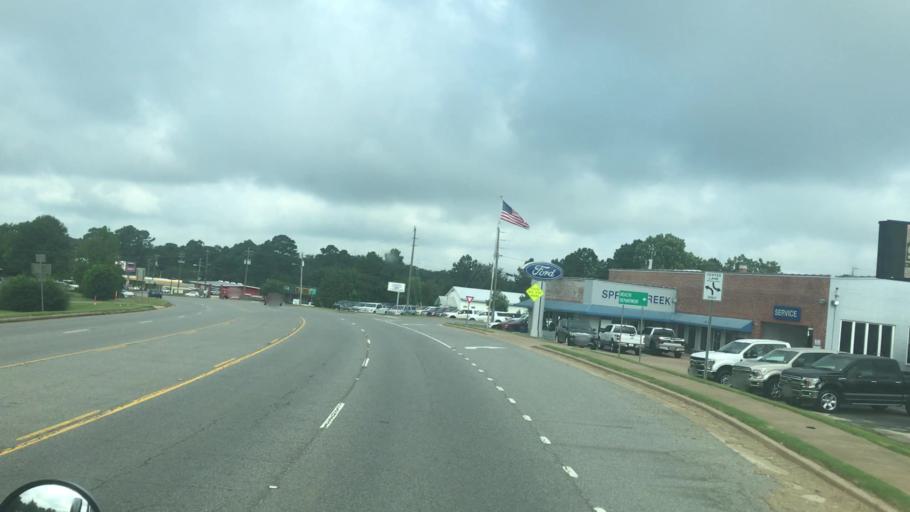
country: US
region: Georgia
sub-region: Miller County
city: Colquitt
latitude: 31.1715
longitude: -84.7374
